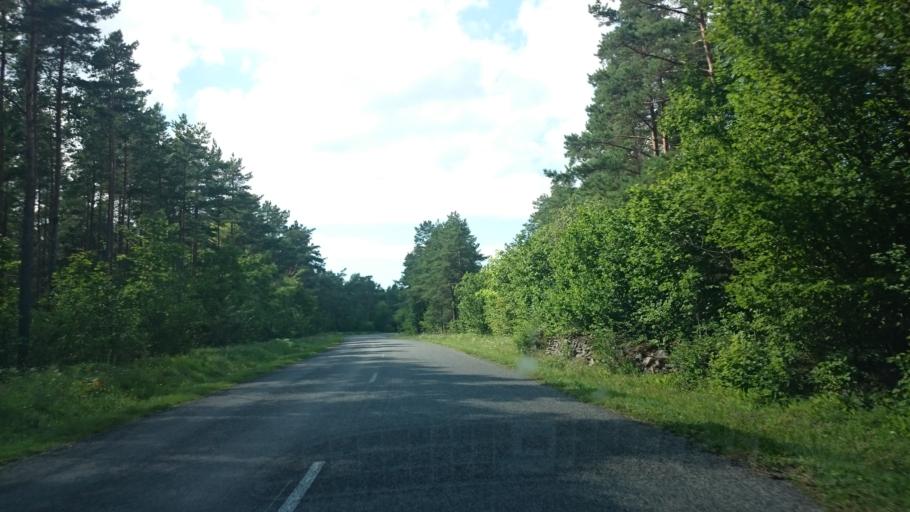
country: EE
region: Saare
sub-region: Orissaare vald
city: Orissaare
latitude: 58.5969
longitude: 22.9932
